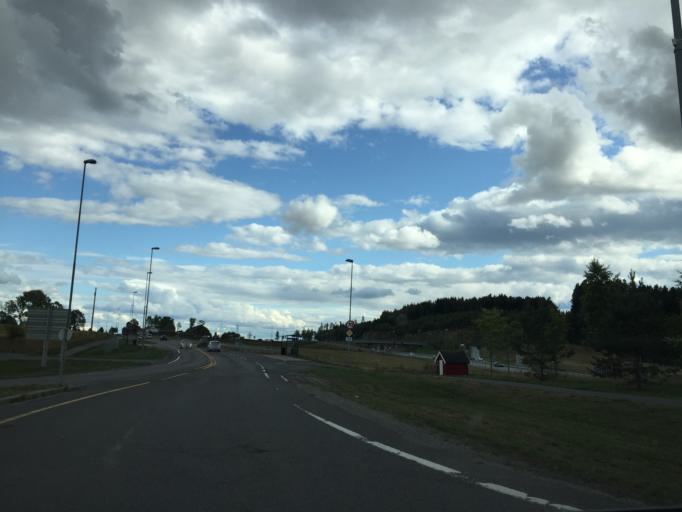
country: NO
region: Ostfold
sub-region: Spydeberg
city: Spydeberg
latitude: 59.5887
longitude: 11.1139
